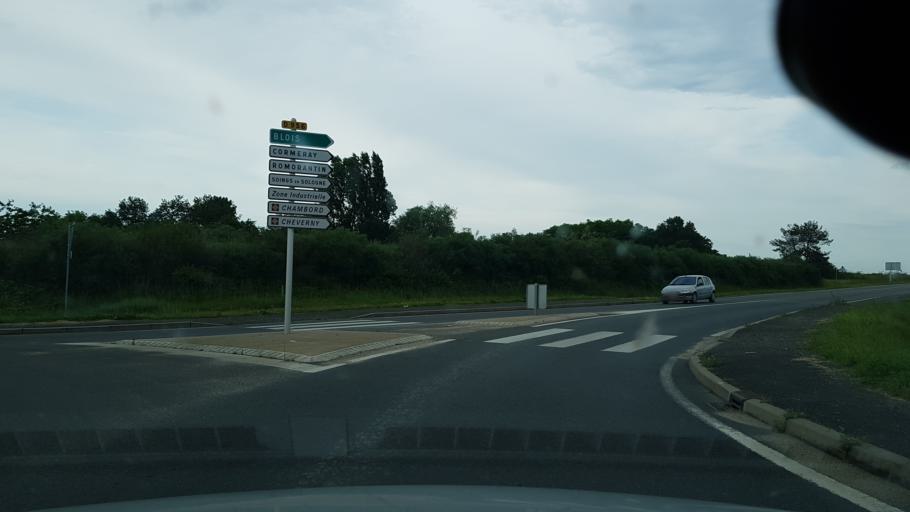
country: FR
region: Centre
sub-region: Departement du Loir-et-Cher
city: Contres
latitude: 47.4088
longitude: 1.4424
